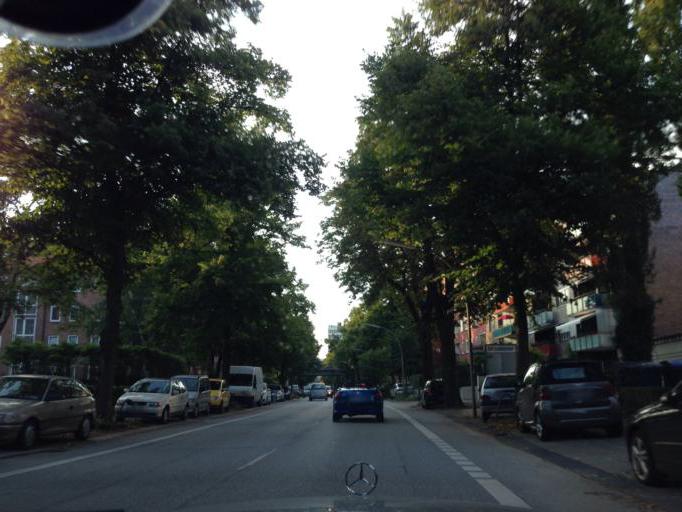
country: DE
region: Hamburg
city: Borgfelde
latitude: 53.5712
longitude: 10.0364
